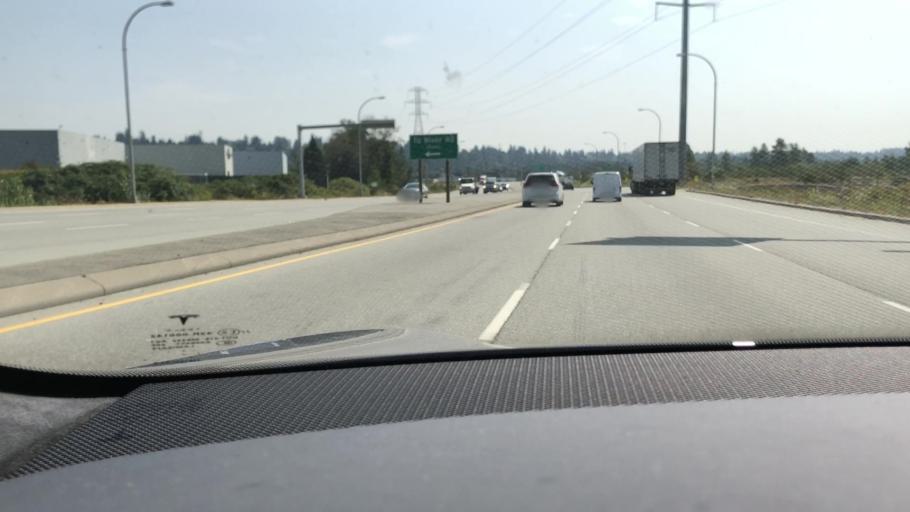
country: CA
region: British Columbia
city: Delta
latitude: 49.1481
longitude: -122.9501
